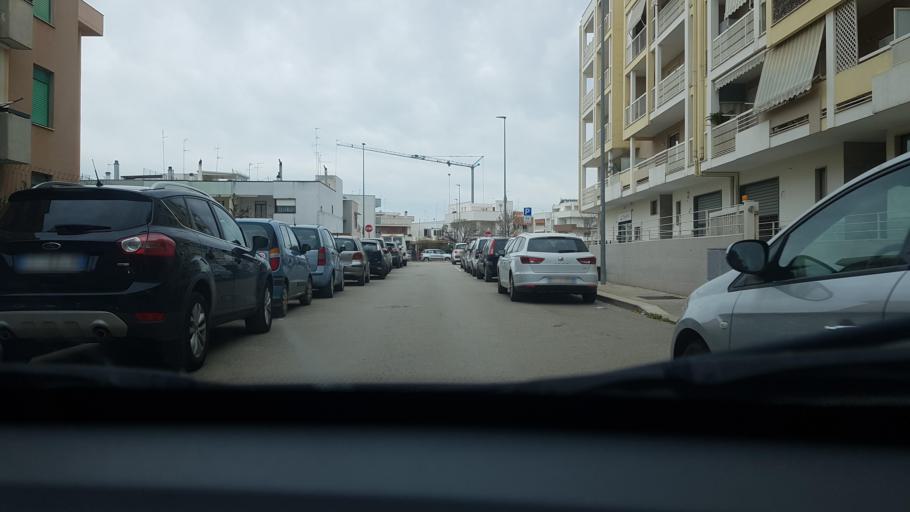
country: IT
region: Apulia
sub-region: Provincia di Bari
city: Noicattaro
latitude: 41.0388
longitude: 16.9851
